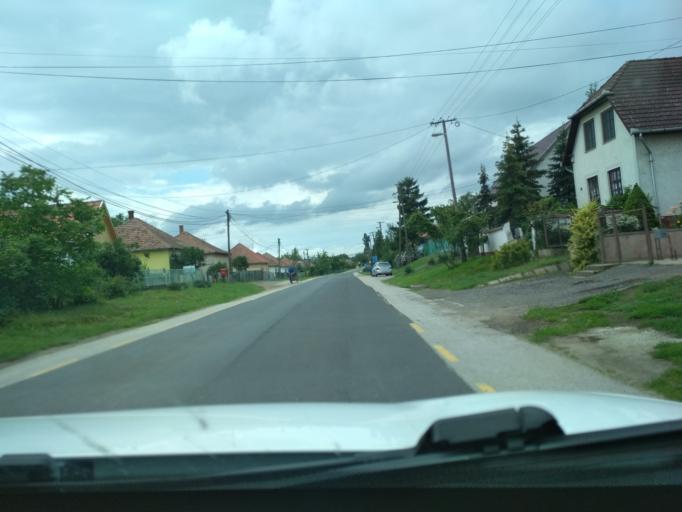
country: HU
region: Jasz-Nagykun-Szolnok
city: Tiszafured
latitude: 47.6105
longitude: 20.7298
